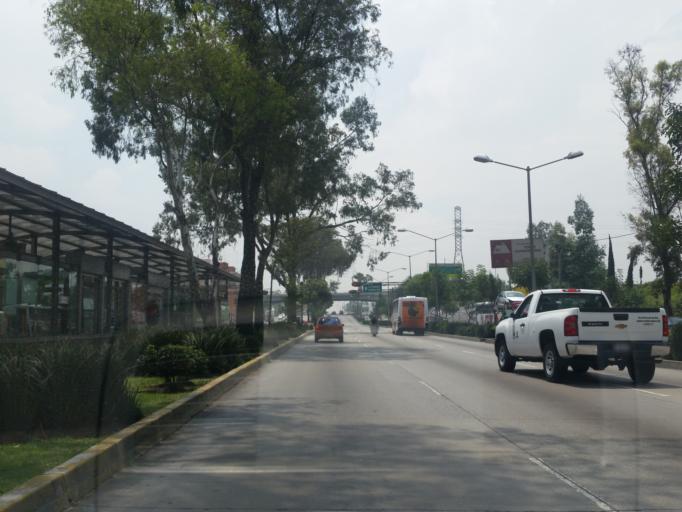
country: MX
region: Mexico City
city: Azcapotzalco
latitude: 19.5157
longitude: -99.1622
